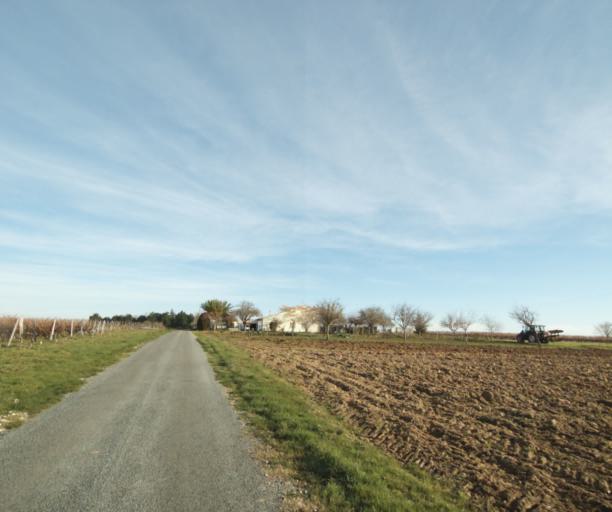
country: FR
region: Poitou-Charentes
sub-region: Departement de la Charente-Maritime
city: Chaniers
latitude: 45.7327
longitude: -0.5239
